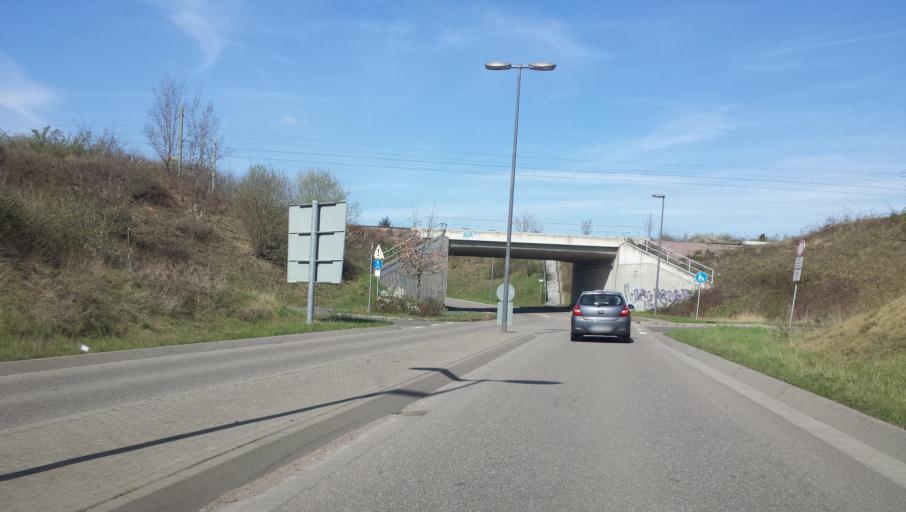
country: DE
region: Rheinland-Pfalz
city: Neustadt
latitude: 49.3592
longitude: 8.1740
